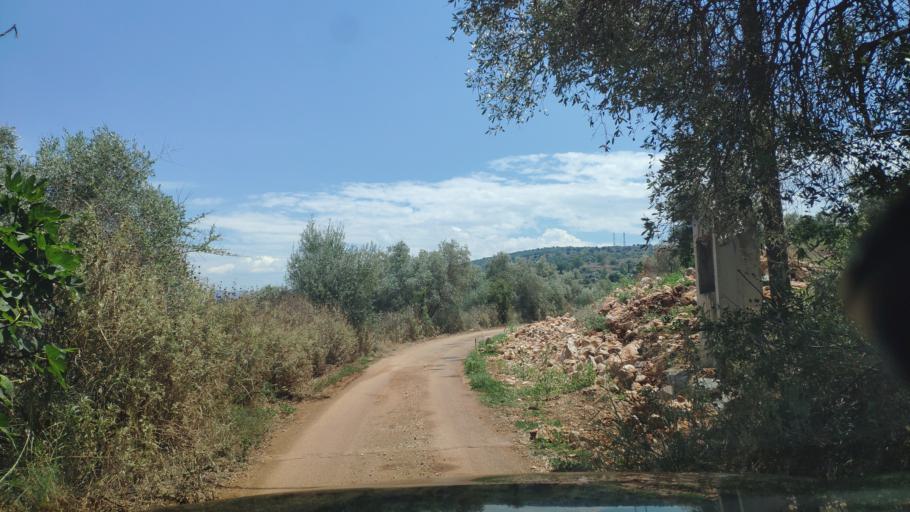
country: GR
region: West Greece
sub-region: Nomos Aitolias kai Akarnanias
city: Amfilochia
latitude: 38.9084
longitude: 21.1066
